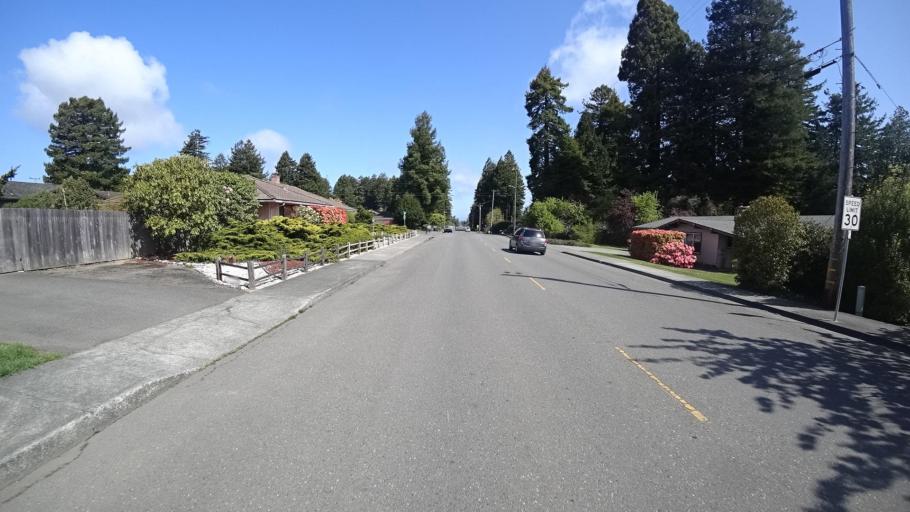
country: US
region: California
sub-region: Humboldt County
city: Cutten
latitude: 40.7764
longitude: -124.1397
